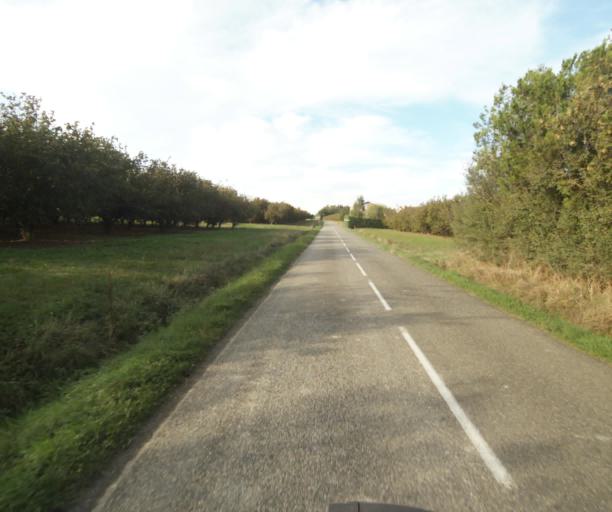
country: FR
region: Midi-Pyrenees
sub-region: Departement du Tarn-et-Garonne
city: Finhan
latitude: 43.8996
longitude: 1.1248
